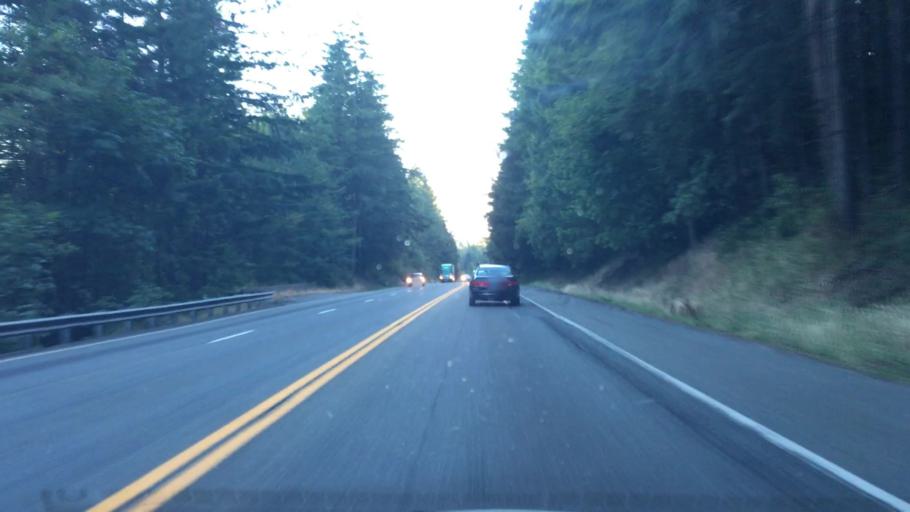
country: US
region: Washington
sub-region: King County
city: Hobart
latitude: 47.4460
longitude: -121.9611
